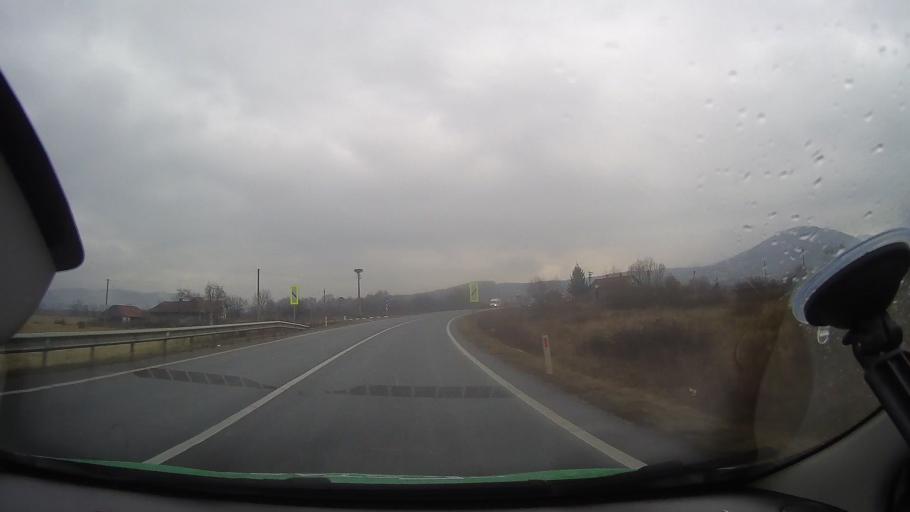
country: RO
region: Hunedoara
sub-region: Comuna Baia de Cris
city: Baia de Cris
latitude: 46.1810
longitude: 22.6796
